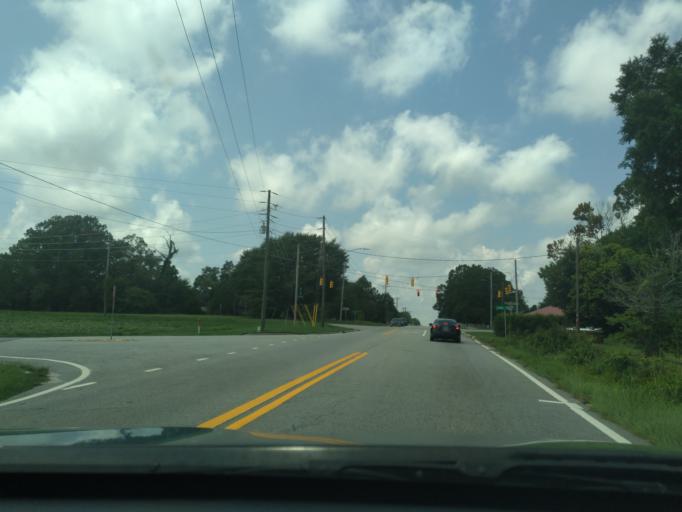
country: US
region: North Carolina
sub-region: Nash County
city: Red Oak
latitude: 36.0111
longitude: -77.8563
